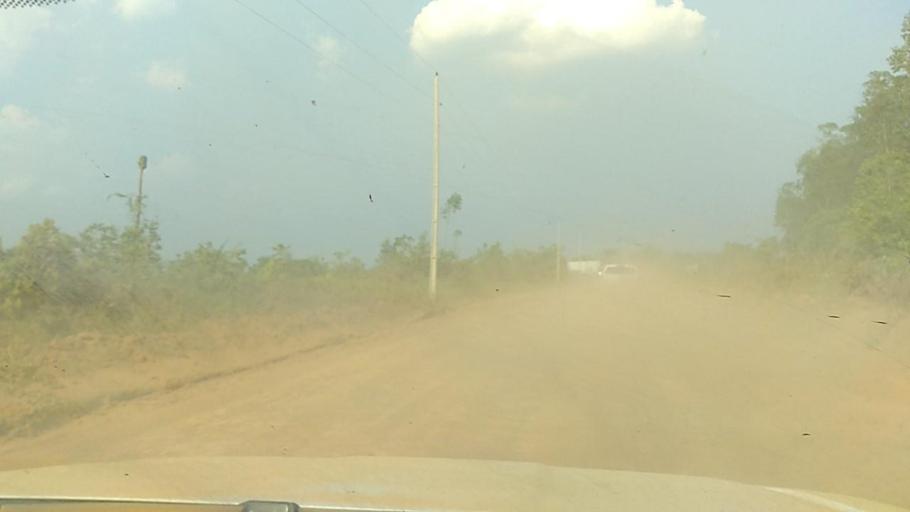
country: BR
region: Rondonia
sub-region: Porto Velho
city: Porto Velho
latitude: -8.6706
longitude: -63.9967
